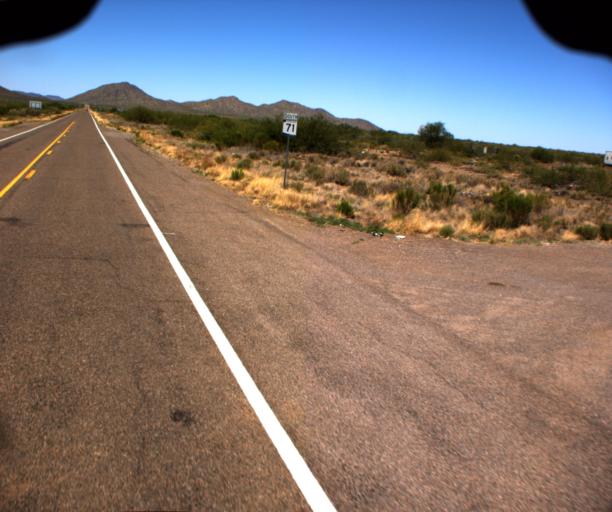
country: US
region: Arizona
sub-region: Yavapai County
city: Congress
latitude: 34.1229
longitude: -112.9519
